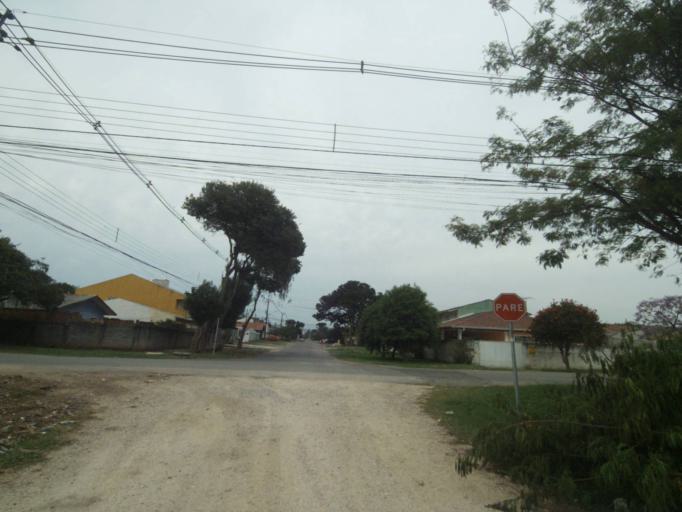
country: BR
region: Parana
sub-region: Pinhais
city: Pinhais
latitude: -25.4159
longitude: -49.1982
